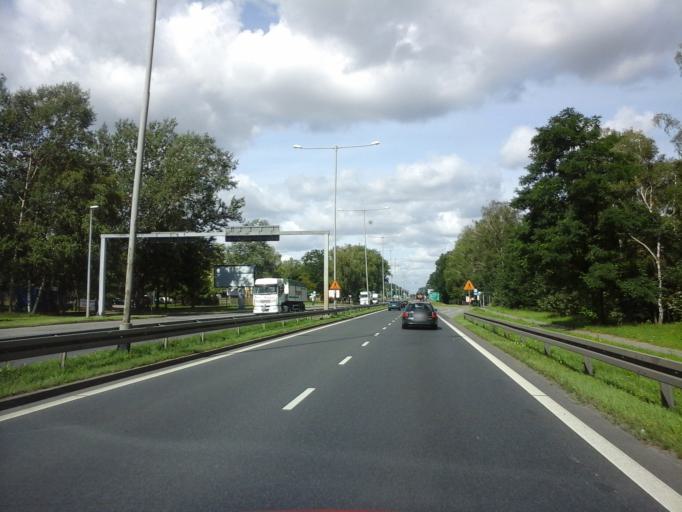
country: PL
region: West Pomeranian Voivodeship
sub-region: Powiat gryfinski
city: Stare Czarnowo
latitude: 53.3624
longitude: 14.7412
